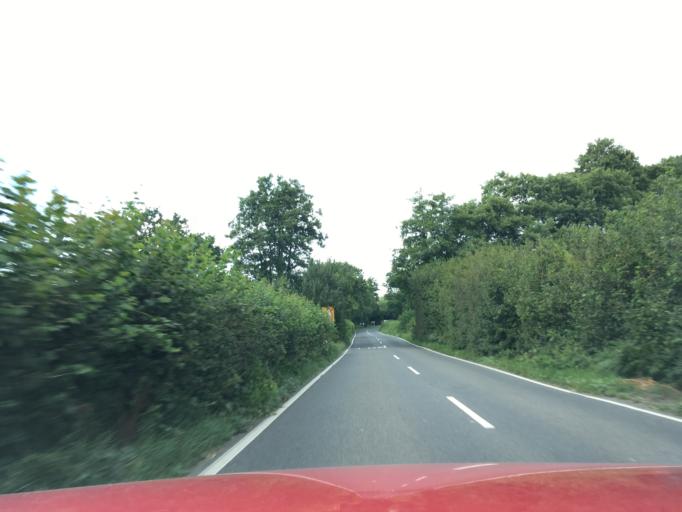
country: GB
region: England
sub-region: East Sussex
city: Crowborough
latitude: 51.1154
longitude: 0.1130
